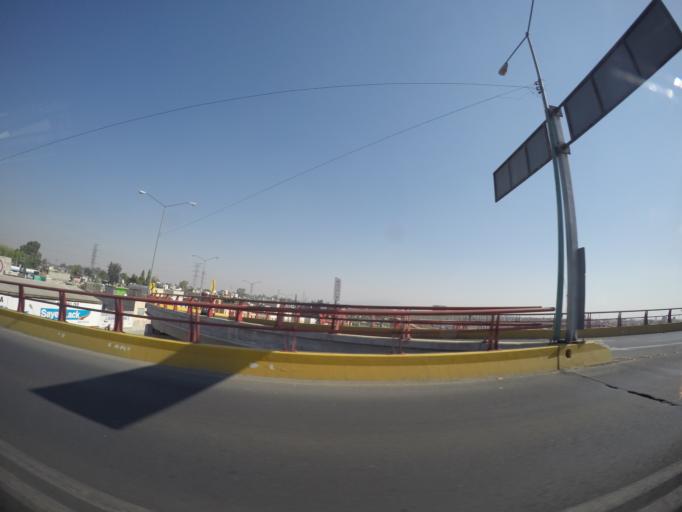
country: MX
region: Mexico
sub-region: Atenco
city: Colonia el Salado
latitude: 19.5879
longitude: -99.0251
